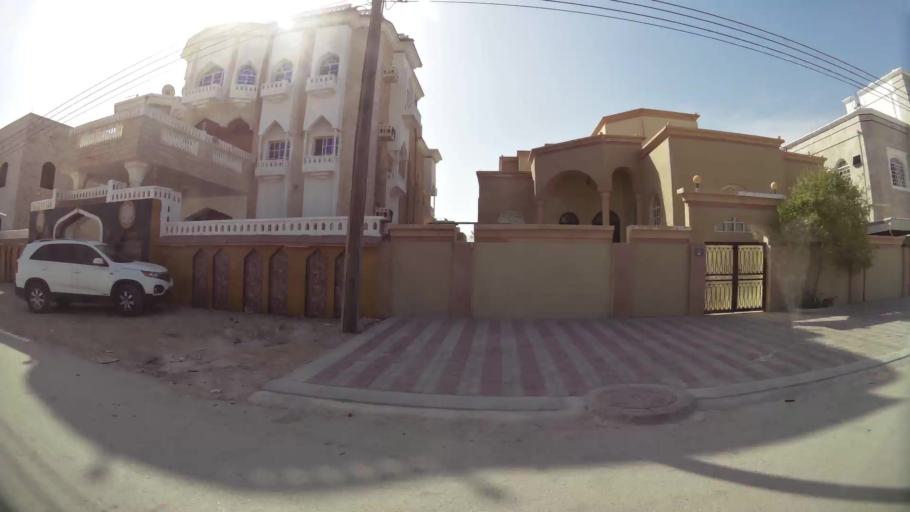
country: OM
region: Zufar
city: Salalah
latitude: 17.0149
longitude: 54.0090
